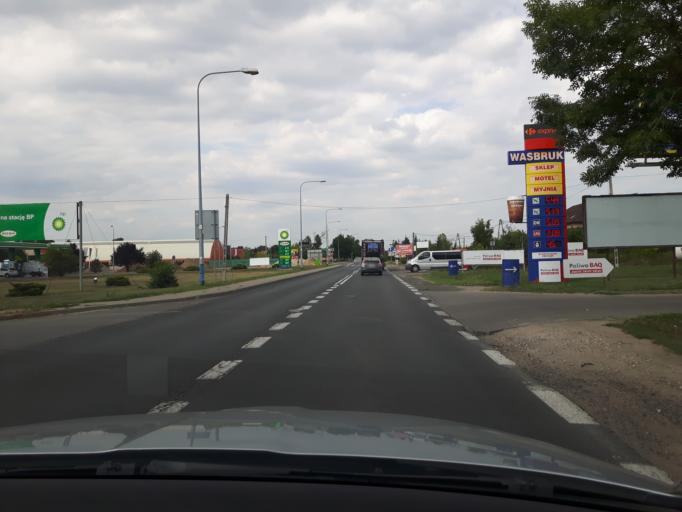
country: PL
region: Masovian Voivodeship
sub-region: Powiat legionowski
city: Stanislawow Pierwszy
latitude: 52.3360
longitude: 21.0295
